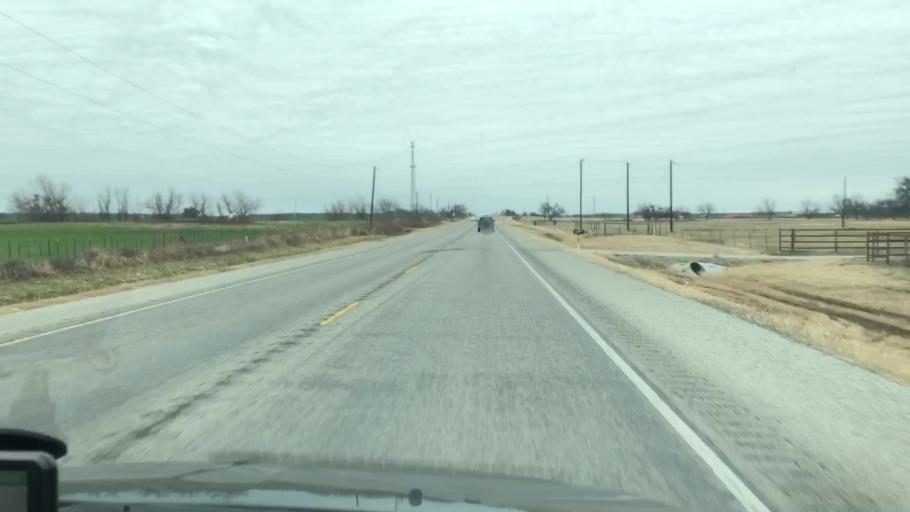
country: US
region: Texas
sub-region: Palo Pinto County
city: Mineral Wells
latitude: 32.9119
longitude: -98.0786
